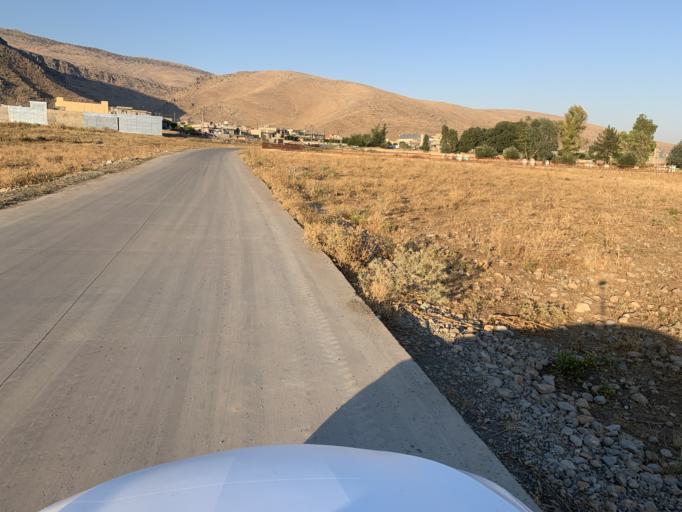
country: IQ
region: As Sulaymaniyah
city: Raniye
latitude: 36.2712
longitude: 44.7564
